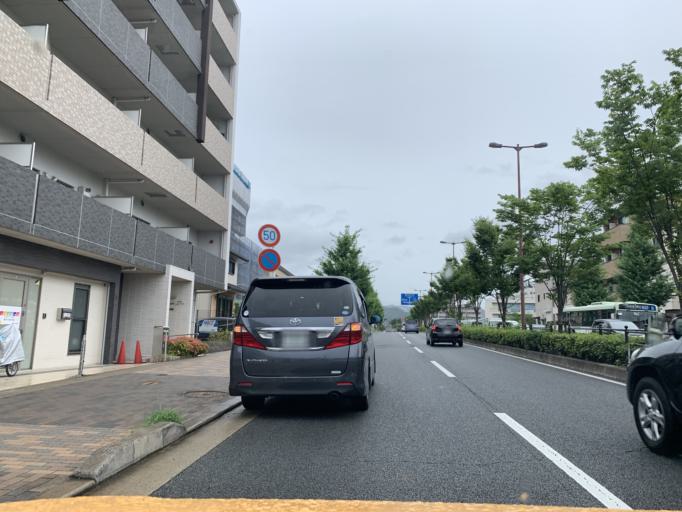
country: JP
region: Kyoto
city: Kyoto
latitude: 35.0087
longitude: 135.7194
